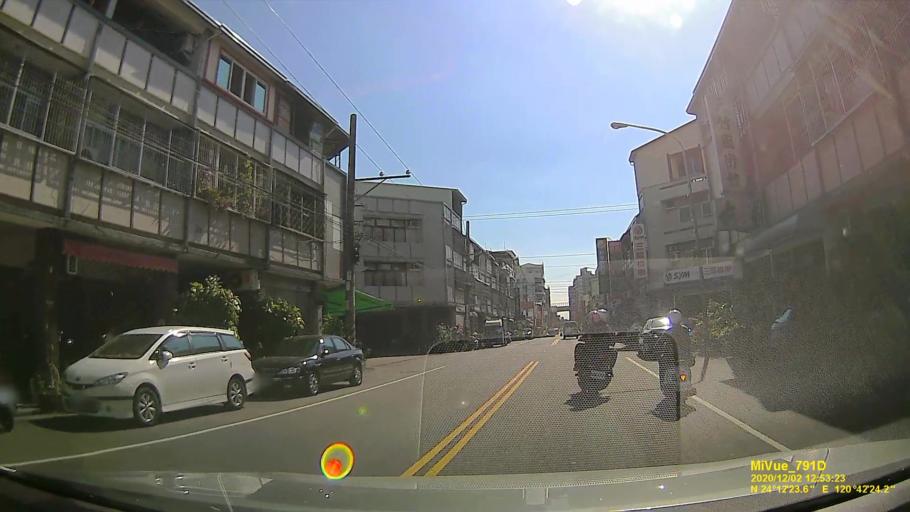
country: TW
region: Taiwan
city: Fengyuan
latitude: 24.2065
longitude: 120.7068
